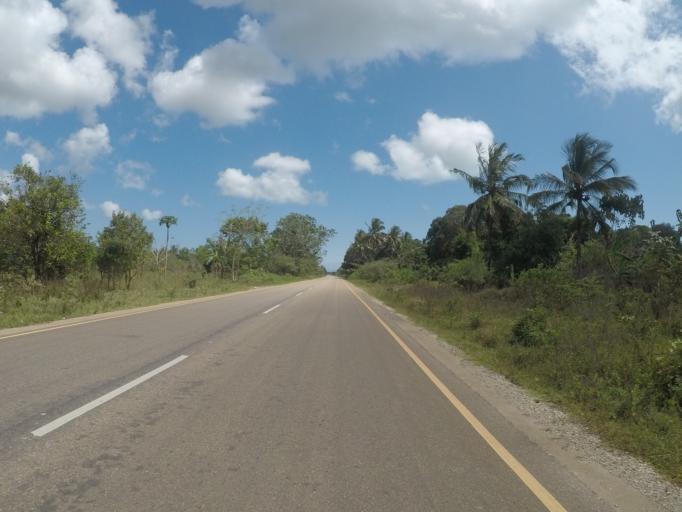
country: TZ
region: Zanzibar Central/South
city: Koani
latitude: -6.2386
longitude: 39.3582
